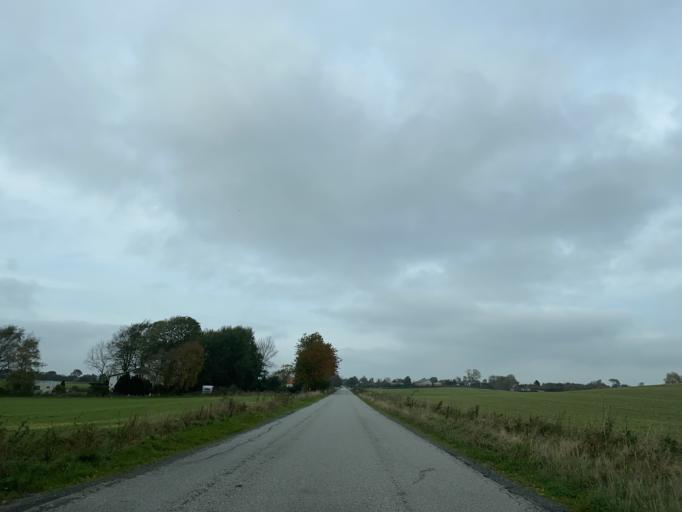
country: DK
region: South Denmark
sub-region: Haderslev Kommune
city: Starup
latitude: 55.1818
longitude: 9.5169
